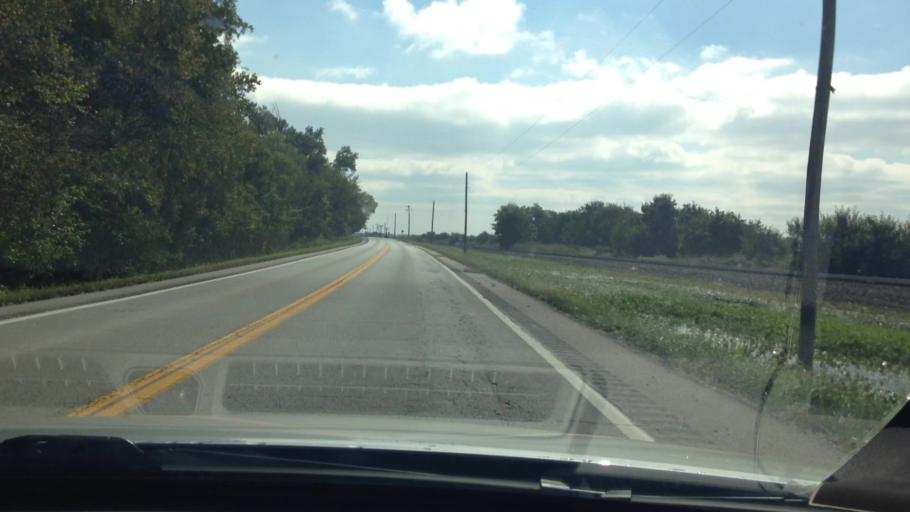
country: US
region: Kansas
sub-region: Leavenworth County
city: Lansing
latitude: 39.3022
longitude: -94.8470
